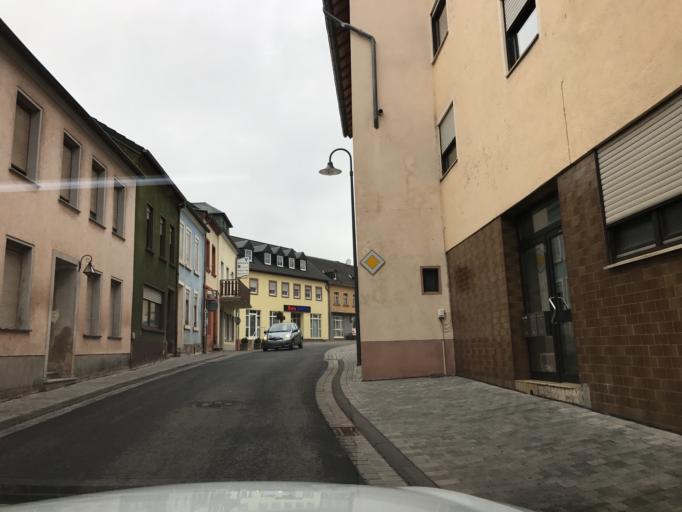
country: DE
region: Rheinland-Pfalz
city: Freudenburg
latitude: 49.5416
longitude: 6.5339
